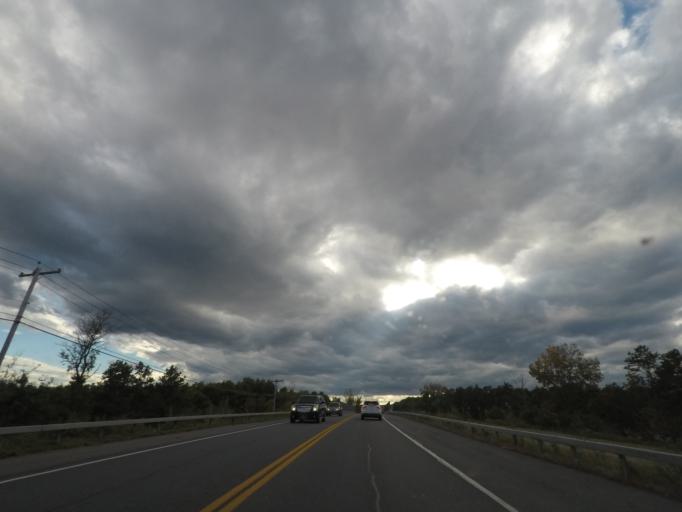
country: US
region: New York
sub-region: Albany County
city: Westmere
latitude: 42.7153
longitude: -73.8682
